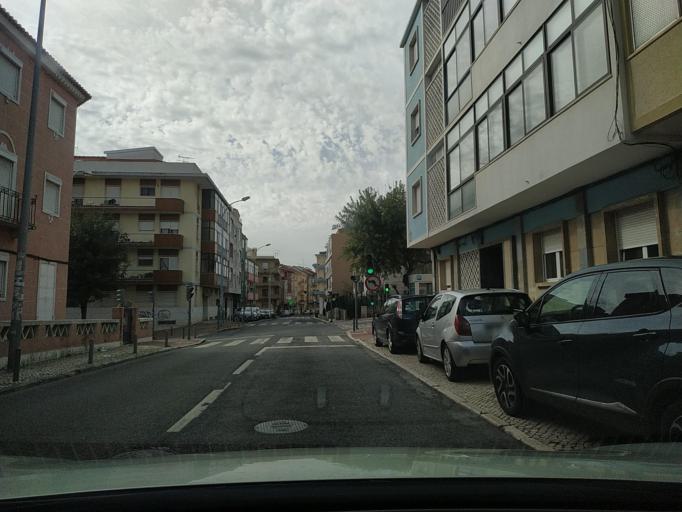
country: PT
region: Lisbon
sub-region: Amadora
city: Amadora
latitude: 38.7630
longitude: -9.2366
